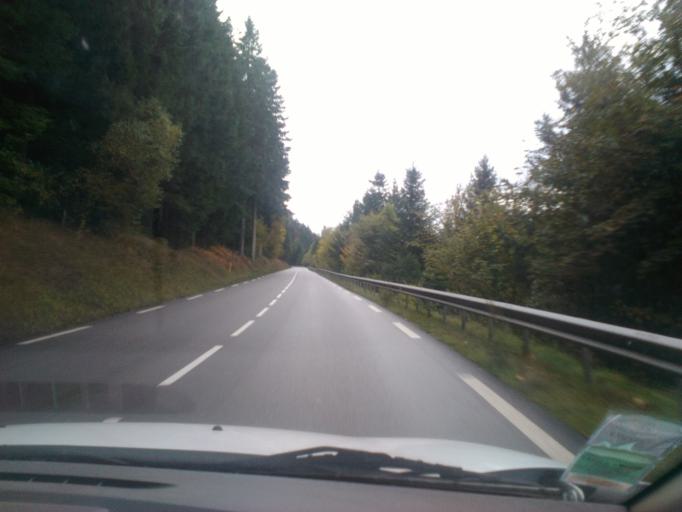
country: FR
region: Lorraine
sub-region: Departement des Vosges
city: Xonrupt-Longemer
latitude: 48.1186
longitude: 6.9105
